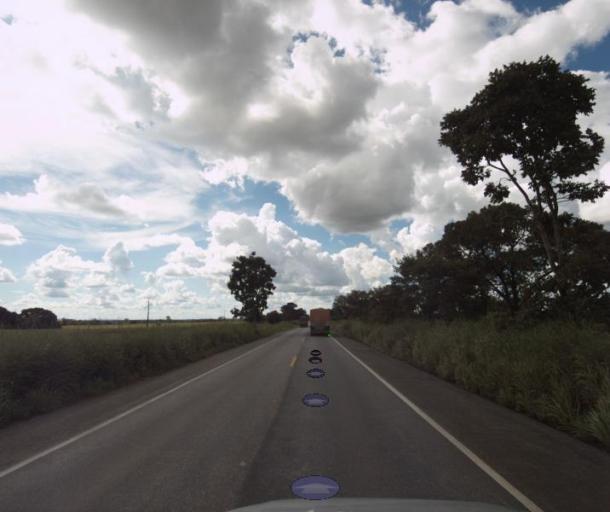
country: BR
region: Goias
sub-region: Porangatu
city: Porangatu
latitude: -13.2846
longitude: -49.1268
